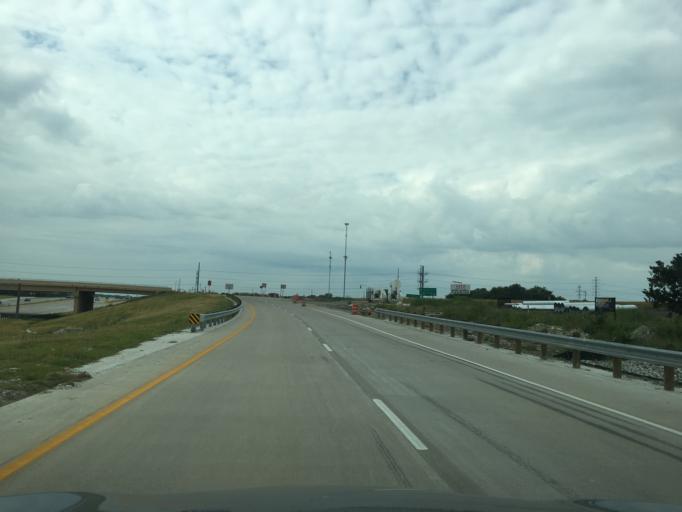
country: US
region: Texas
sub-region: Collin County
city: Melissa
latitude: 33.3209
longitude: -96.5910
